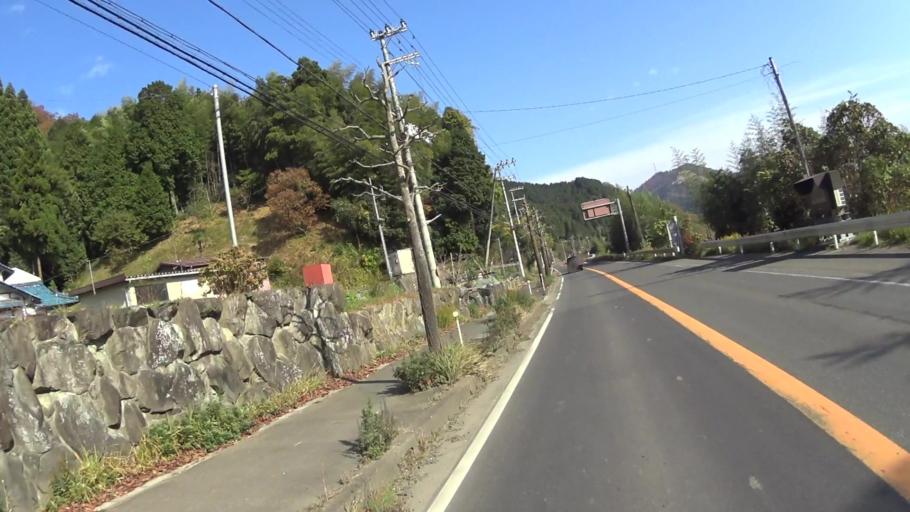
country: JP
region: Kyoto
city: Miyazu
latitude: 35.4270
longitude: 135.2205
